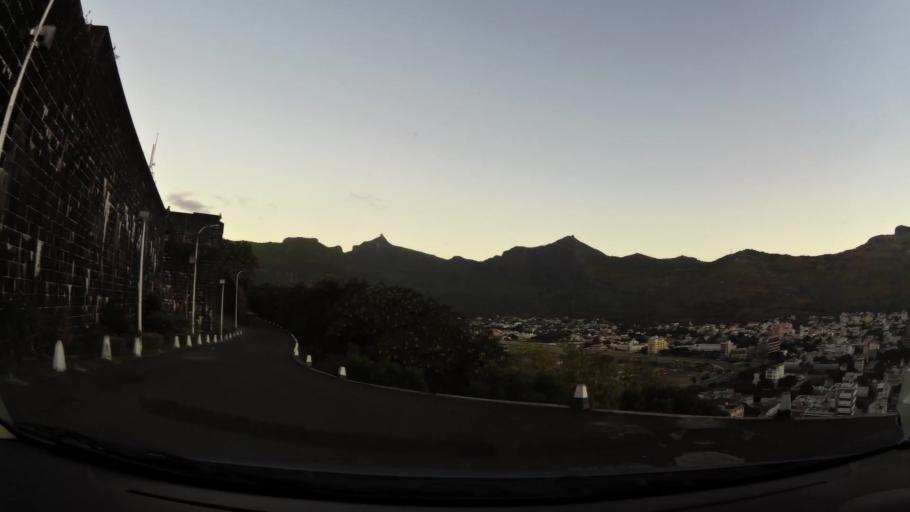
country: MU
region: Port Louis
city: Port Louis
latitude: -20.1638
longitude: 57.5100
